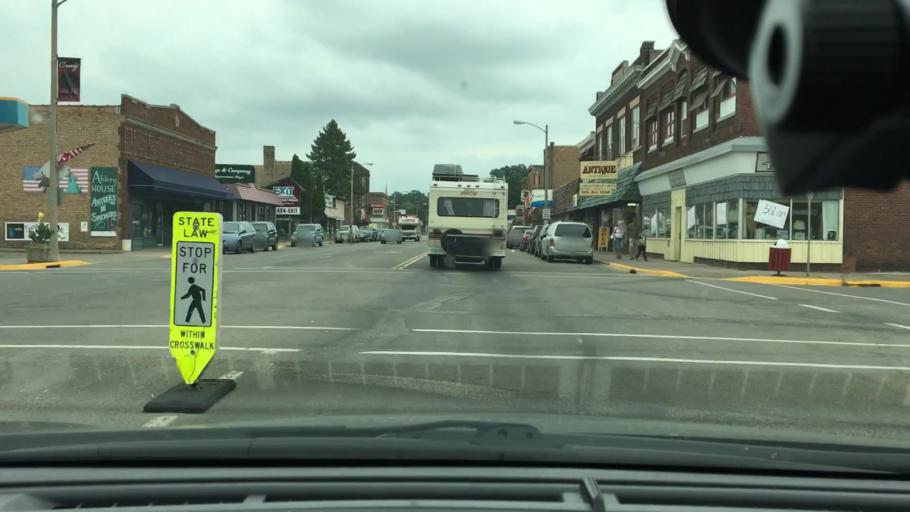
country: US
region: Minnesota
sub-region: Crow Wing County
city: Crosby
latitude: 46.4824
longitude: -93.9544
